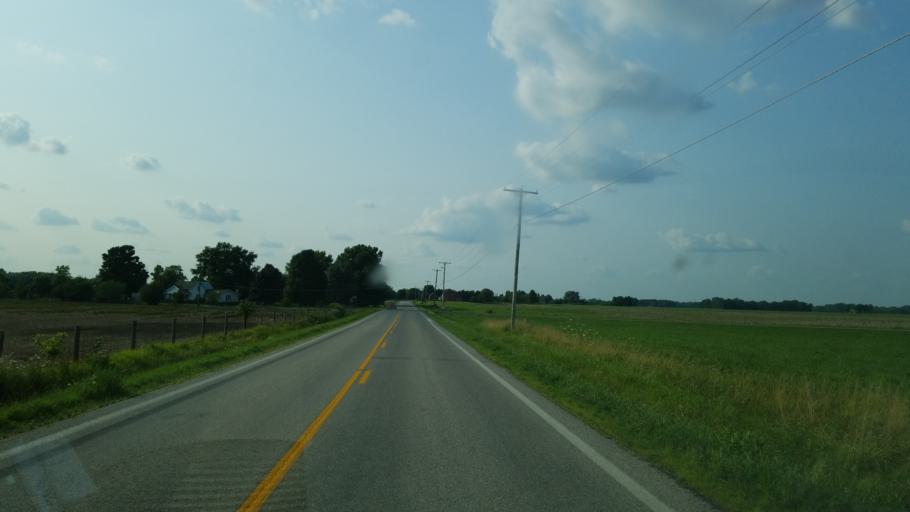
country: US
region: Ohio
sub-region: Union County
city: Richwood
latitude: 40.3632
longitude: -83.2620
